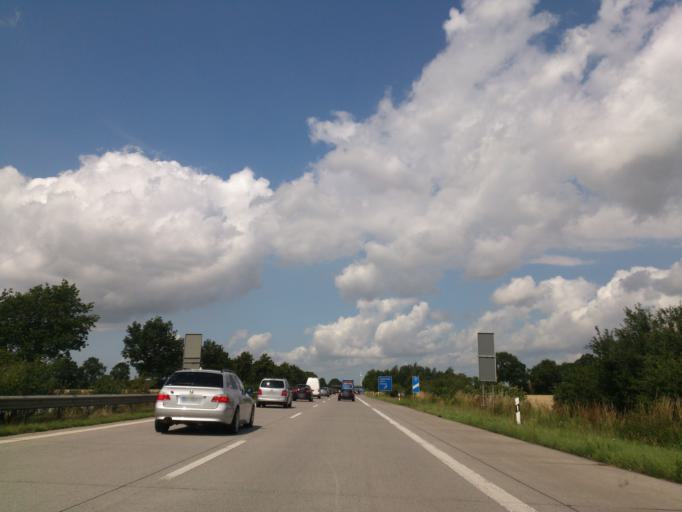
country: DE
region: Schleswig-Holstein
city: Hohenfelde
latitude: 53.8395
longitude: 9.6092
